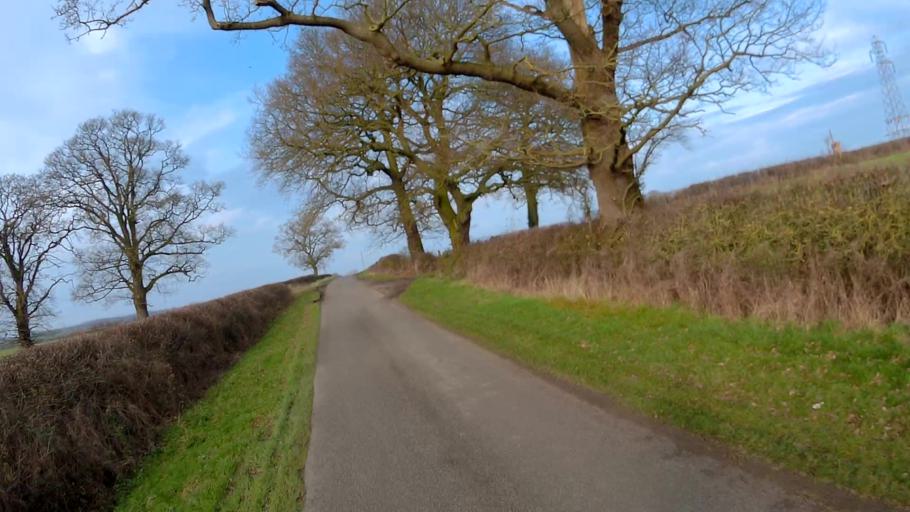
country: GB
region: England
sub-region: Lincolnshire
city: Bourne
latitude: 52.7657
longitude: -0.4211
